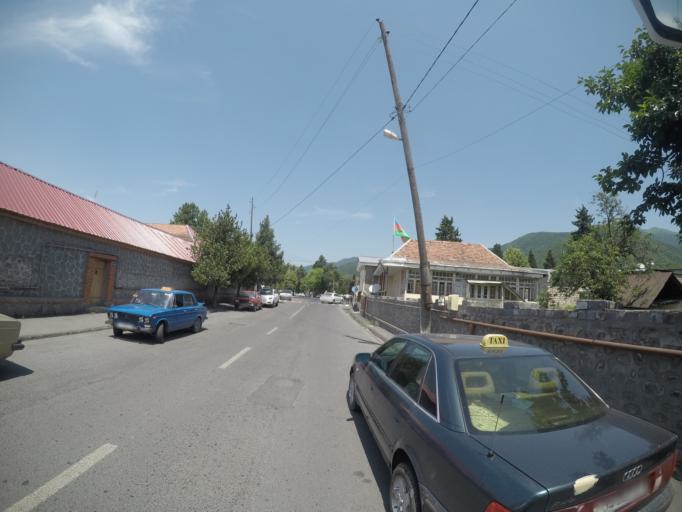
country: AZ
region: Qakh Rayon
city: Qax
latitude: 41.4189
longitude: 46.9185
